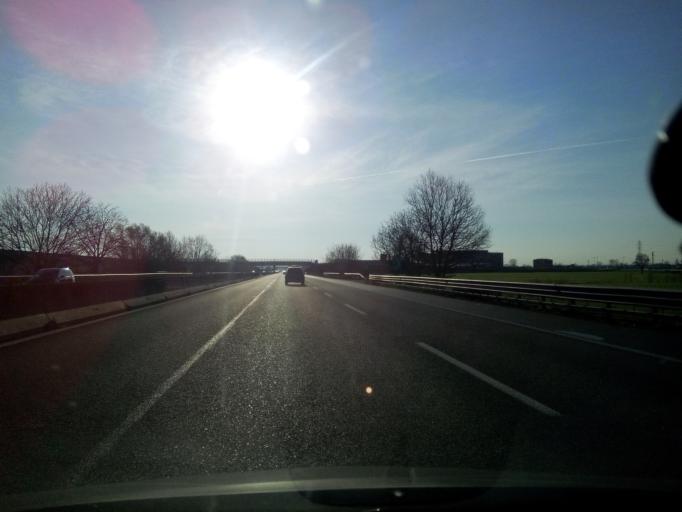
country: IT
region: Emilia-Romagna
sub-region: Provincia di Parma
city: Fontanellato
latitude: 44.8754
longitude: 10.1766
